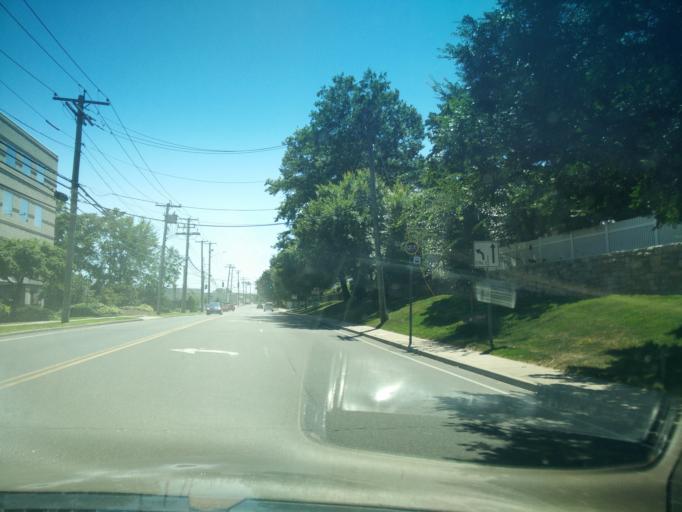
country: US
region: Connecticut
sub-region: Fairfield County
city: Bridgeport
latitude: 41.1623
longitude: -73.2360
